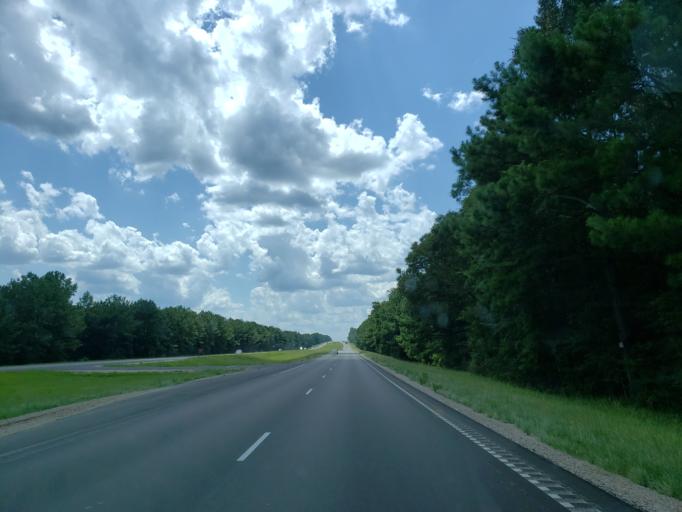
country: US
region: Mississippi
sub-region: Perry County
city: New Augusta
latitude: 31.2112
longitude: -89.1341
